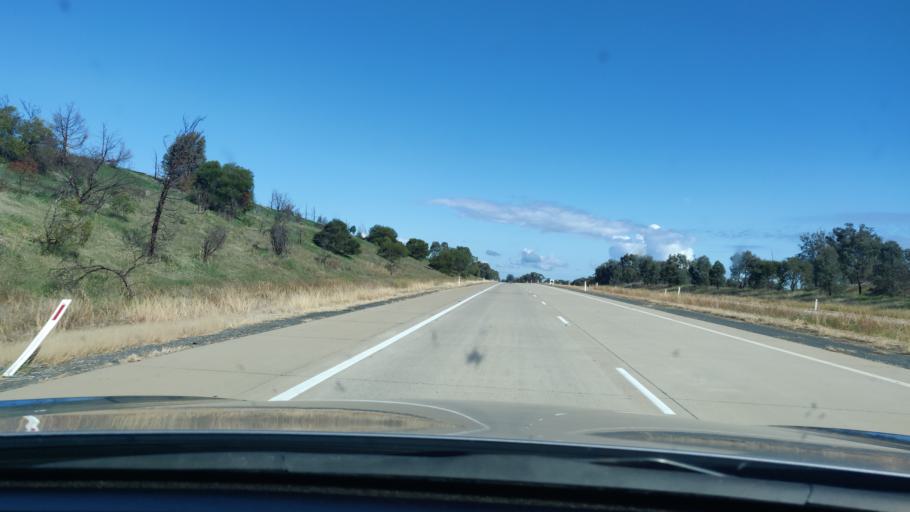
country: AU
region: New South Wales
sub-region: Greater Hume Shire
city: Holbrook
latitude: -35.6824
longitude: 147.3629
